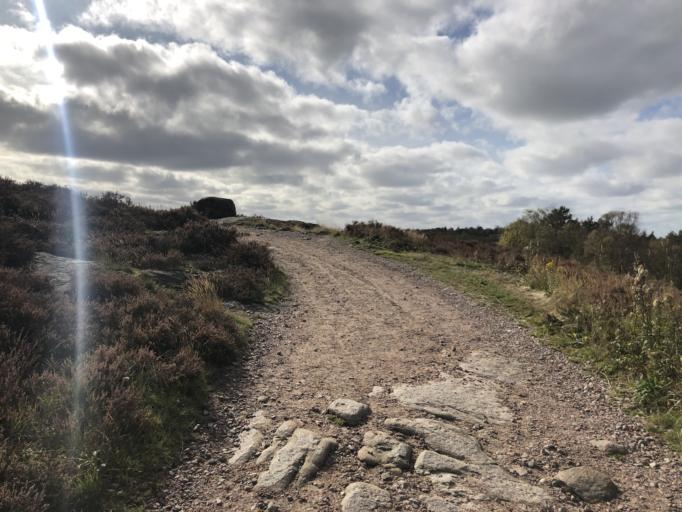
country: SE
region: Vaestra Goetaland
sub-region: Goteborg
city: Goeteborg
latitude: 57.6704
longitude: 11.9592
